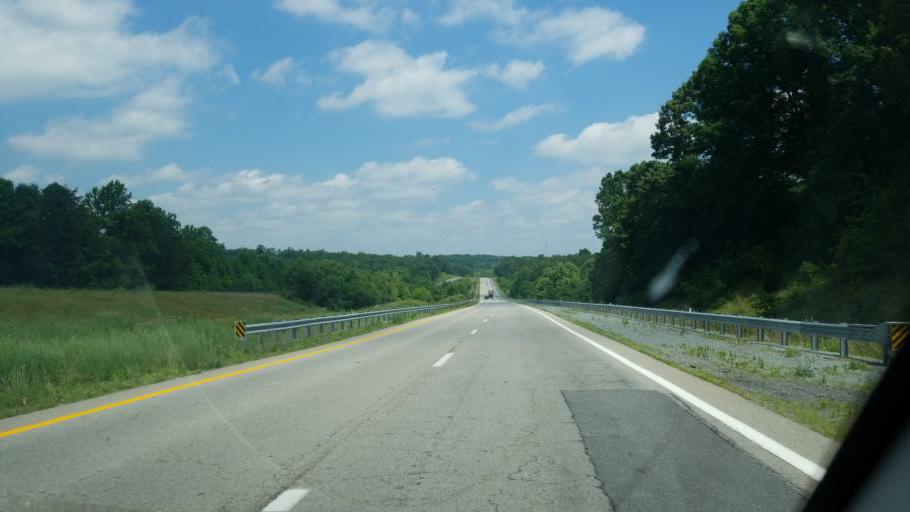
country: US
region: Virginia
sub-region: Pittsylvania County
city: Motley
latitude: 37.0922
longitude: -79.3318
